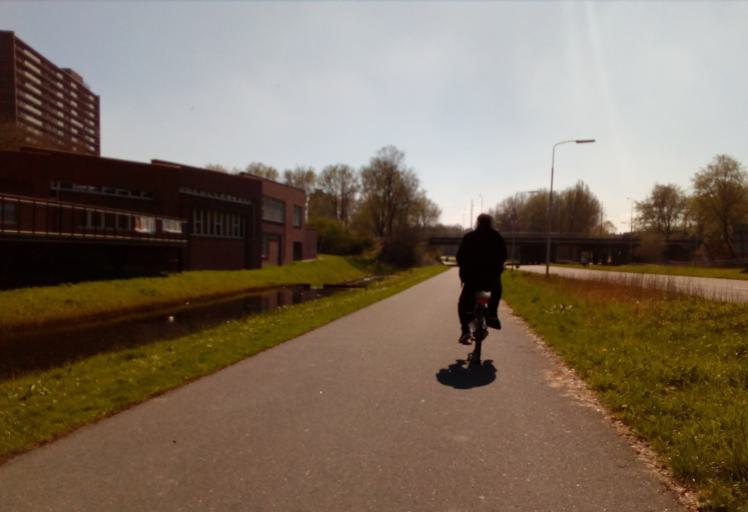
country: NL
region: South Holland
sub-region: Gemeente Delft
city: Delft
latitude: 51.9975
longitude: 4.3490
